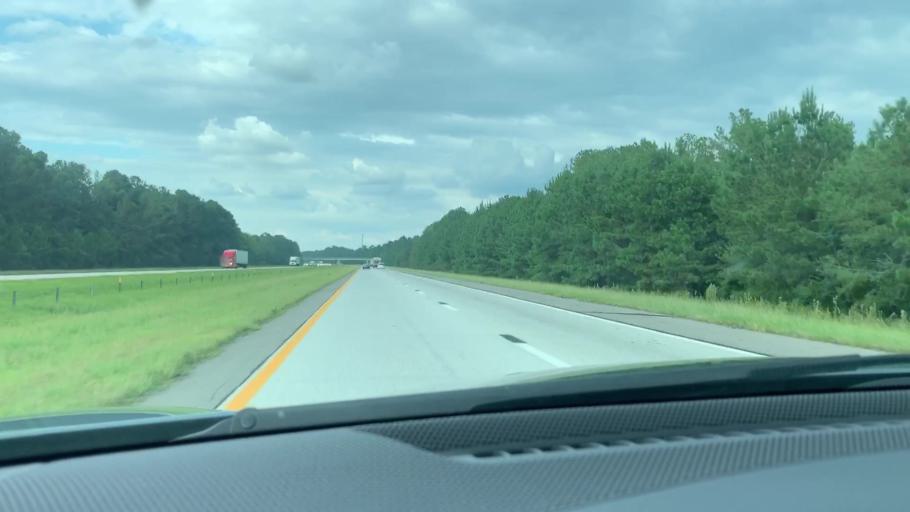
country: US
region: South Carolina
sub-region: Dorchester County
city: Saint George
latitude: 33.2886
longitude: -80.5606
